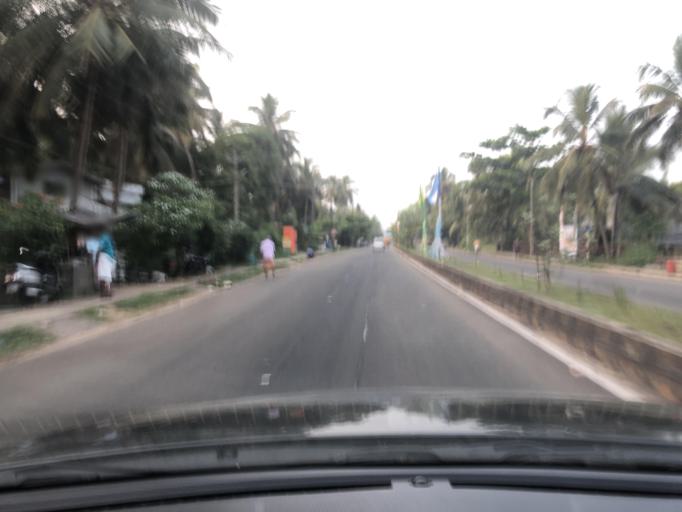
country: IN
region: Kerala
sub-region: Kozhikode
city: Kozhikode
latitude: 11.2966
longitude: 75.7565
